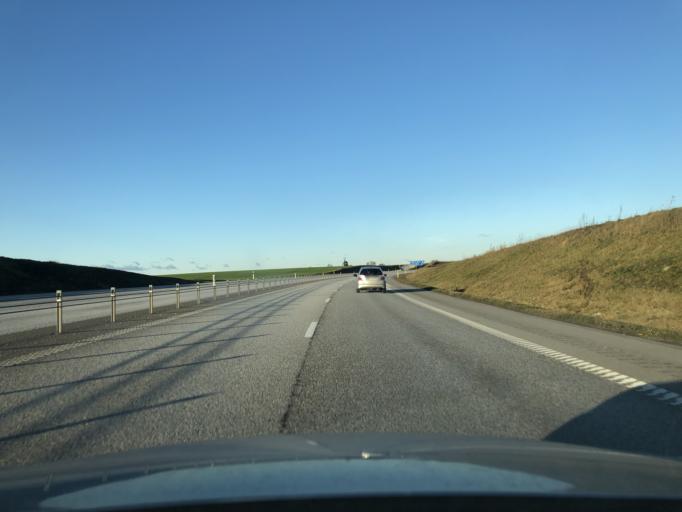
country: SE
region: Skane
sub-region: Trelleborgs Kommun
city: Skare
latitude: 55.4033
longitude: 13.0640
